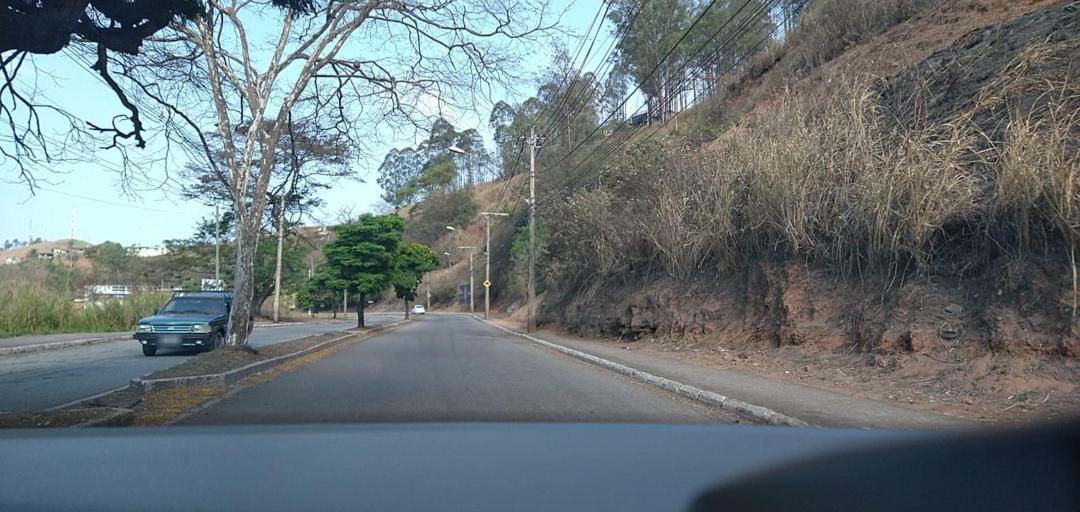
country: BR
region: Minas Gerais
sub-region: Joao Monlevade
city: Joao Monlevade
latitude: -19.8192
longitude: -43.1414
